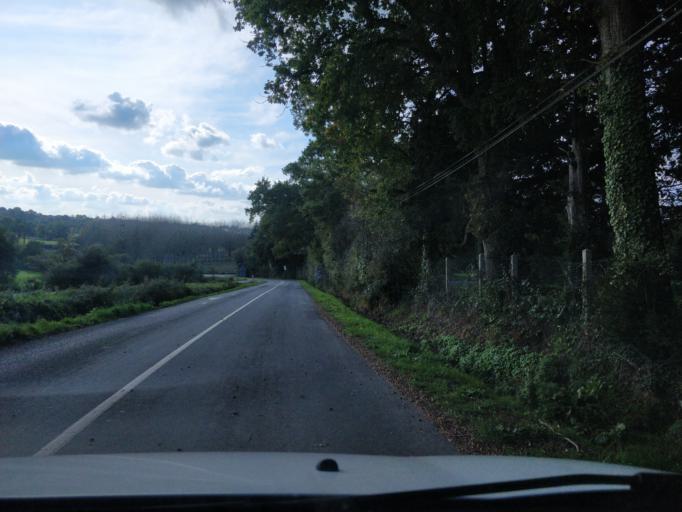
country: FR
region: Brittany
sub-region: Departement d'Ille-et-Vilaine
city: La Bouexiere
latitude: 48.1974
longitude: -1.4219
